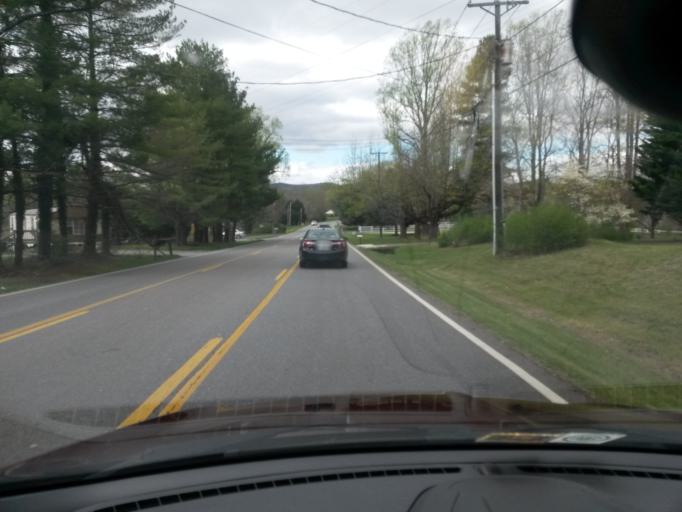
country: US
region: Virginia
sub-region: City of Lynchburg
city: West Lynchburg
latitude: 37.4424
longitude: -79.2389
